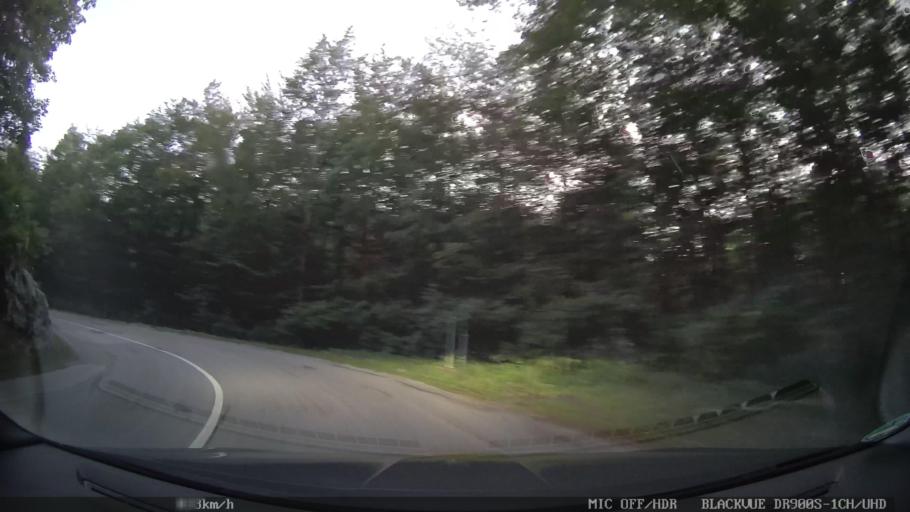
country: HR
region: Primorsko-Goranska
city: Novi Vinodolski
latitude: 45.2012
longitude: 14.8778
